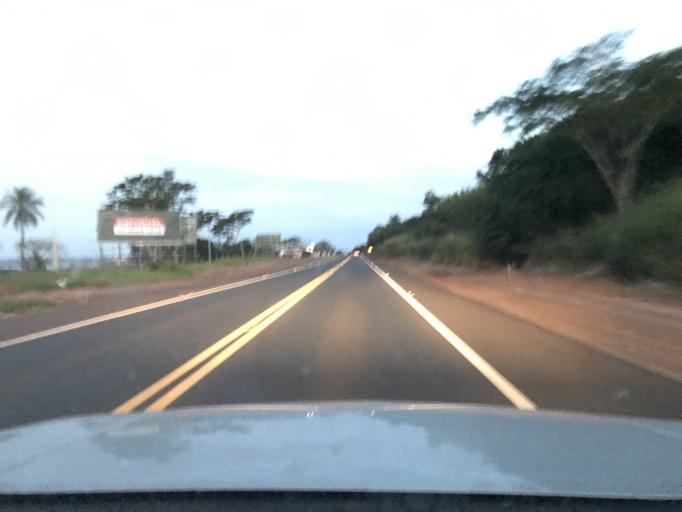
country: PY
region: Canindeyu
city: Salto del Guaira
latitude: -24.0269
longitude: -54.2889
